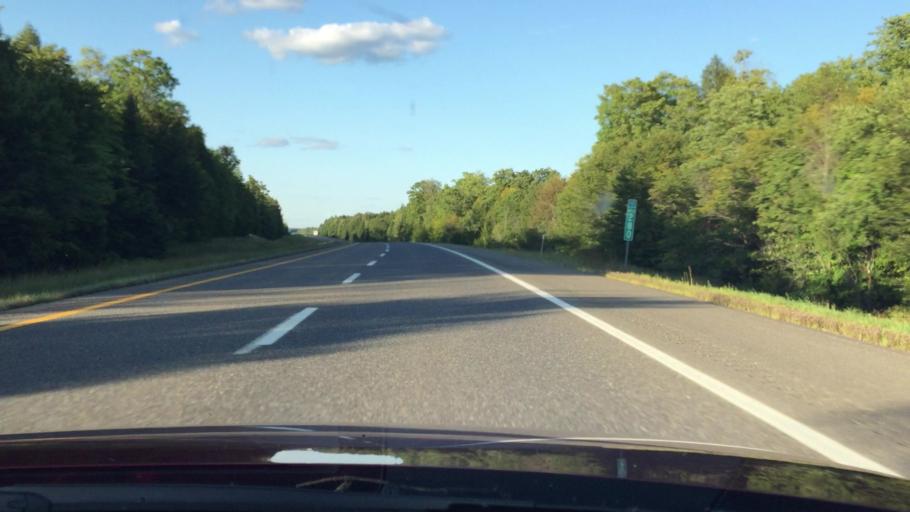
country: US
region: Maine
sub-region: Penobscot County
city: Patten
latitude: 46.0513
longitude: -68.2424
